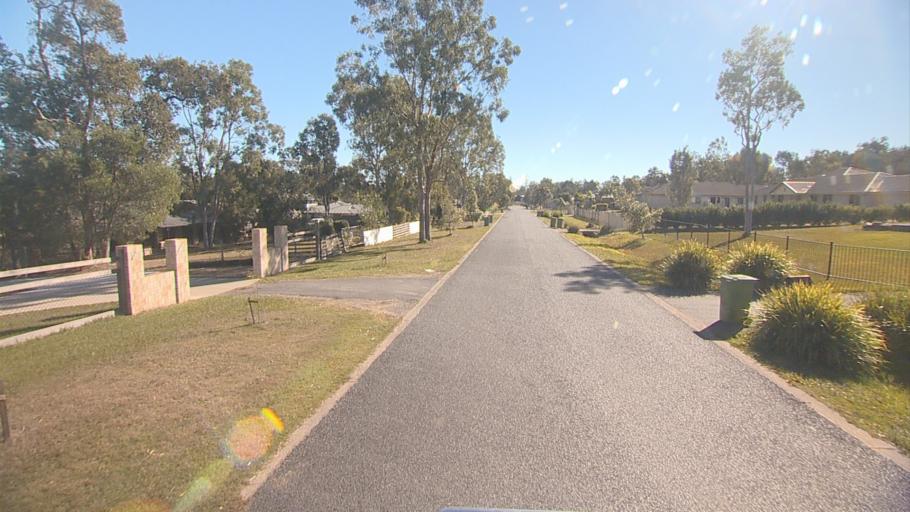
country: AU
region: Queensland
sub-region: Logan
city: North Maclean
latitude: -27.7398
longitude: 152.9558
